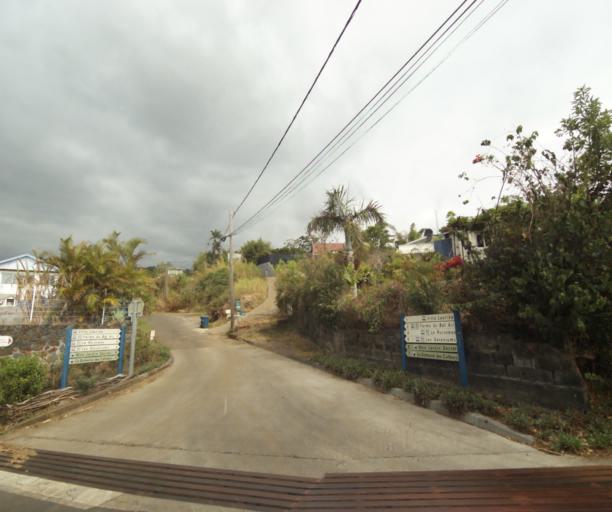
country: RE
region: Reunion
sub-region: Reunion
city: Saint-Paul
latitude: -21.0304
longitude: 55.3107
